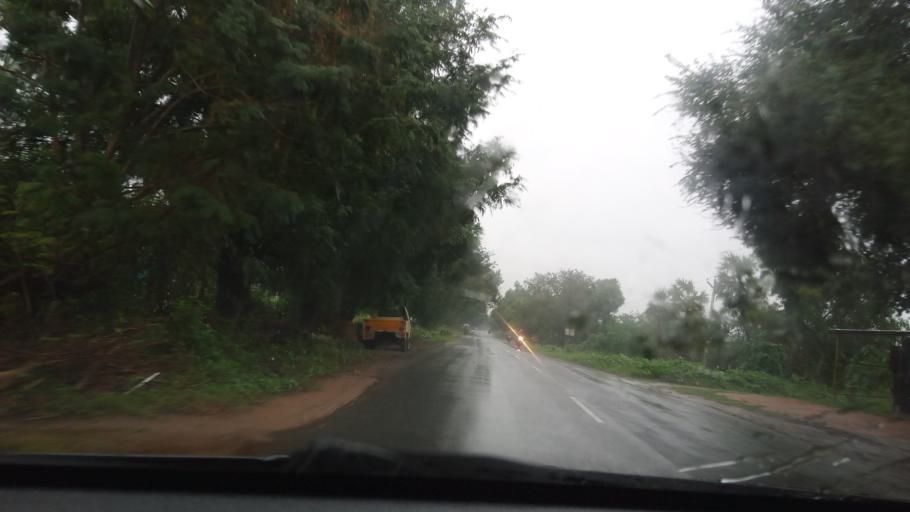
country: IN
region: Tamil Nadu
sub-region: Vellore
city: Walajapet
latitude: 12.8499
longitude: 79.3897
